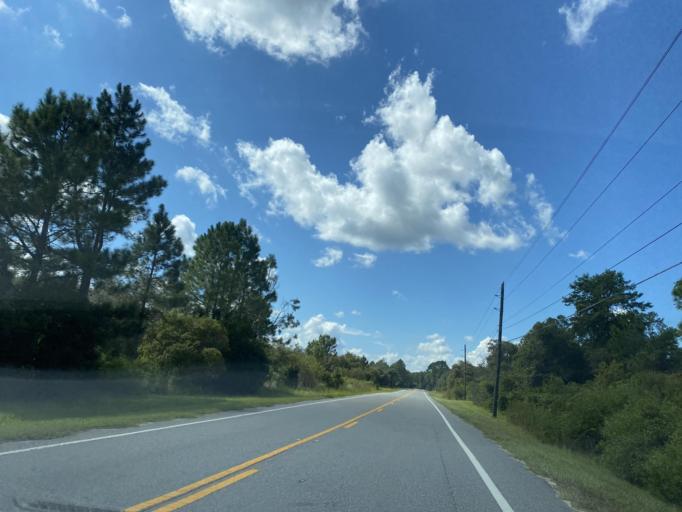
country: US
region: Florida
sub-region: Lake County
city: Lake Mack-Forest Hills
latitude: 29.0062
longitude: -81.4417
